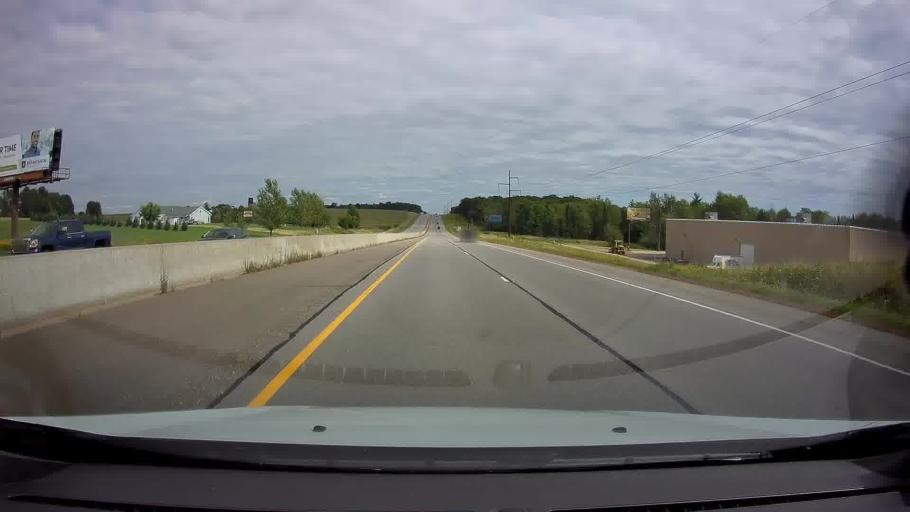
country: US
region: Wisconsin
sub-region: Marathon County
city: Marathon
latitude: 44.9441
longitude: -89.8338
